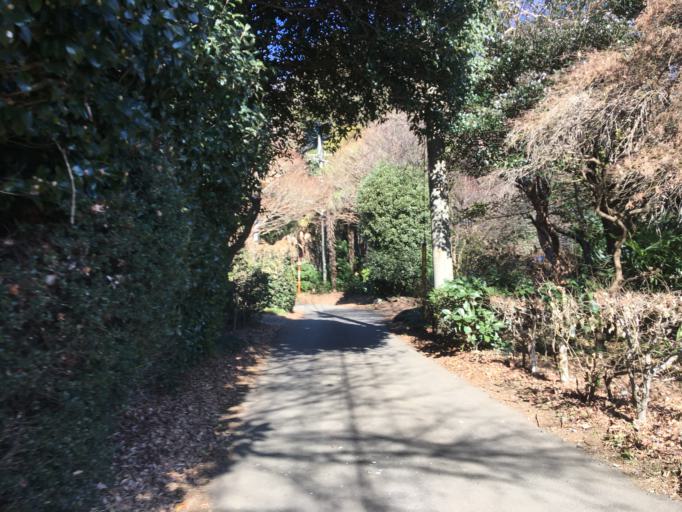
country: JP
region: Saitama
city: Oi
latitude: 35.8145
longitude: 139.5397
